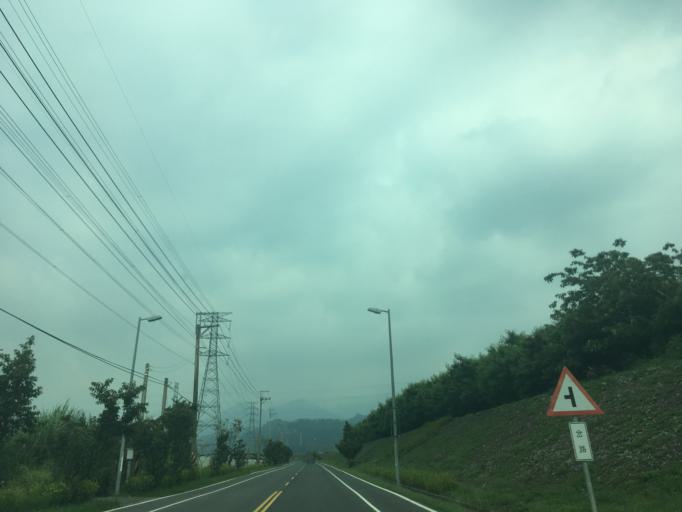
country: TW
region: Taiwan
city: Fengyuan
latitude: 24.2901
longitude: 120.8468
